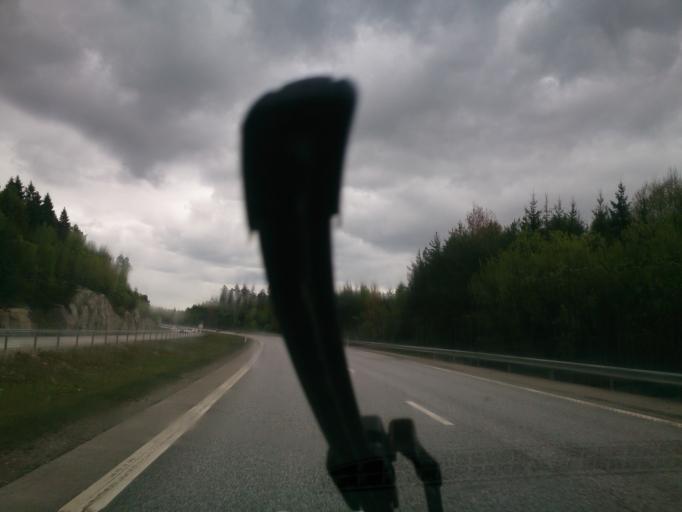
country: SE
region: Soedermanland
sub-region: Trosa Kommun
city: Vagnharad
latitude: 58.9737
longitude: 17.5223
